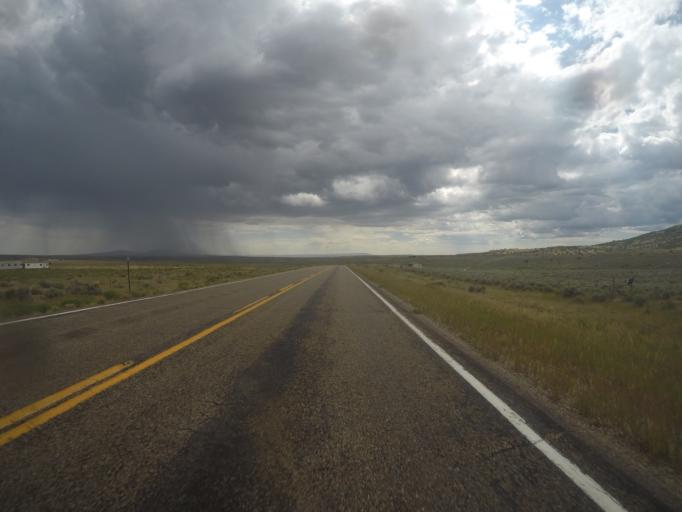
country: US
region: Utah
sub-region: Daggett County
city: Manila
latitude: 41.0267
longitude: -109.8834
